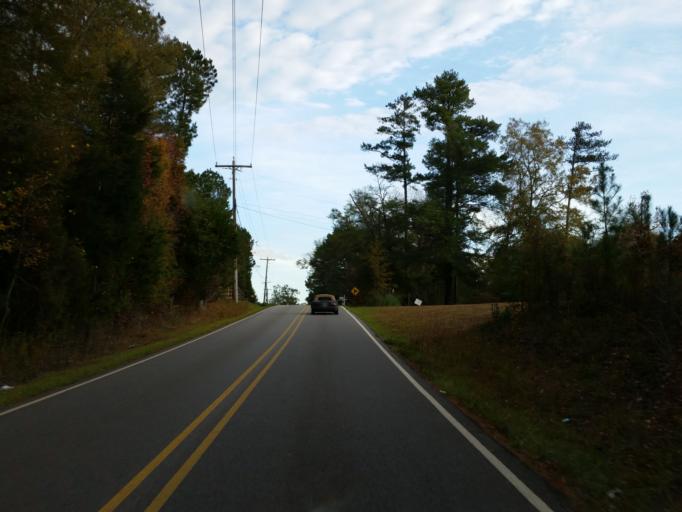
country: US
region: Mississippi
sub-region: Lauderdale County
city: Marion
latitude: 32.4061
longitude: -88.6031
